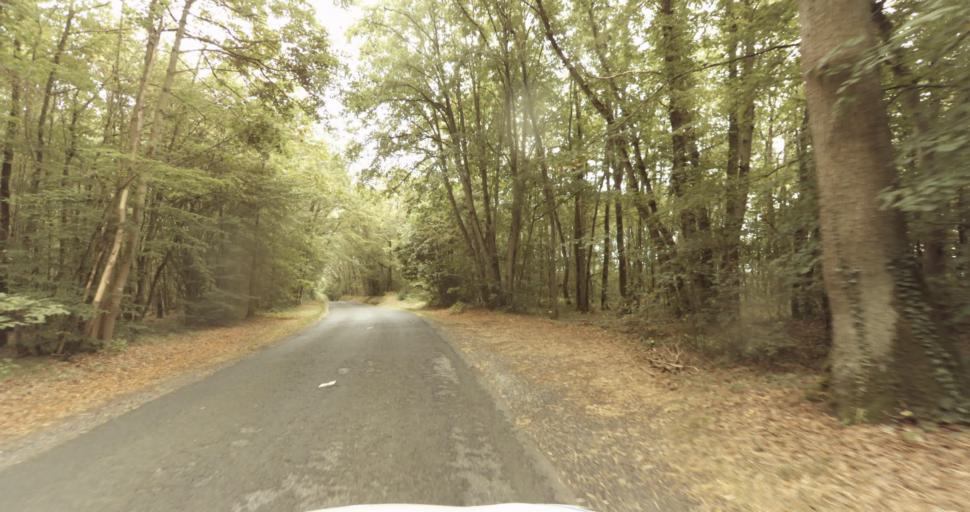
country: FR
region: Centre
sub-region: Departement d'Eure-et-Loir
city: Vert-en-Drouais
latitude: 48.7674
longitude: 1.3111
